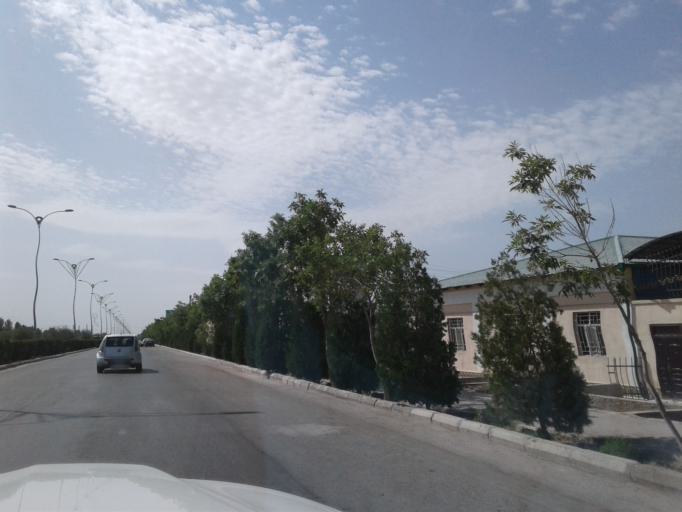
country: TM
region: Dasoguz
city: Dasoguz
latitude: 41.8305
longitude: 59.9435
